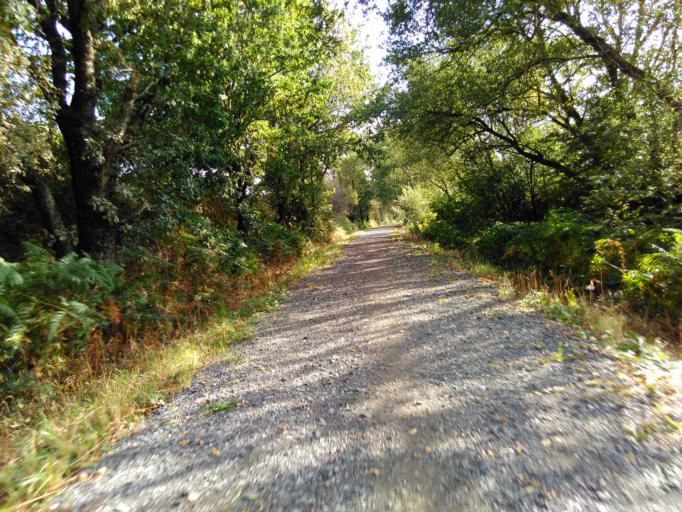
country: BE
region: Wallonia
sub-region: Province du Luxembourg
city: Neufchateau
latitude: 49.9187
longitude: 5.4088
